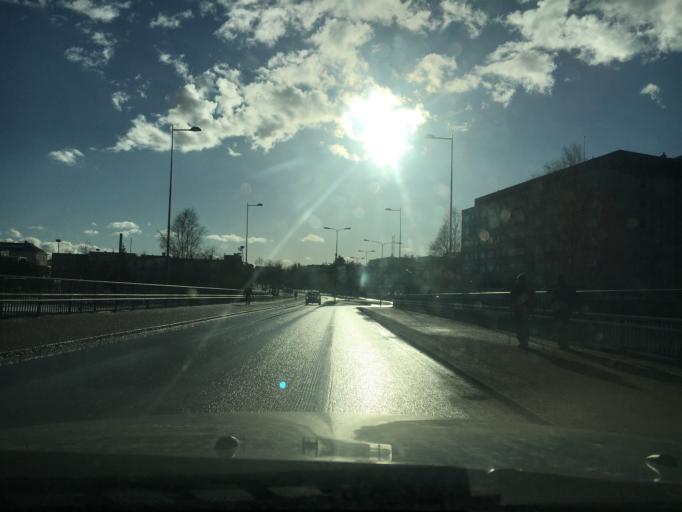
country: FI
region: Kainuu
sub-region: Kajaani
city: Kajaani
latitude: 64.2257
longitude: 27.7374
